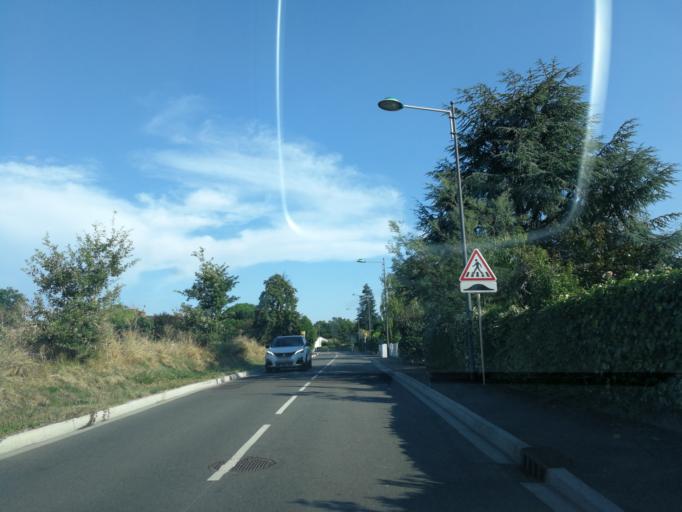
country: FR
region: Midi-Pyrenees
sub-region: Departement de la Haute-Garonne
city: Balma
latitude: 43.6227
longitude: 1.4993
